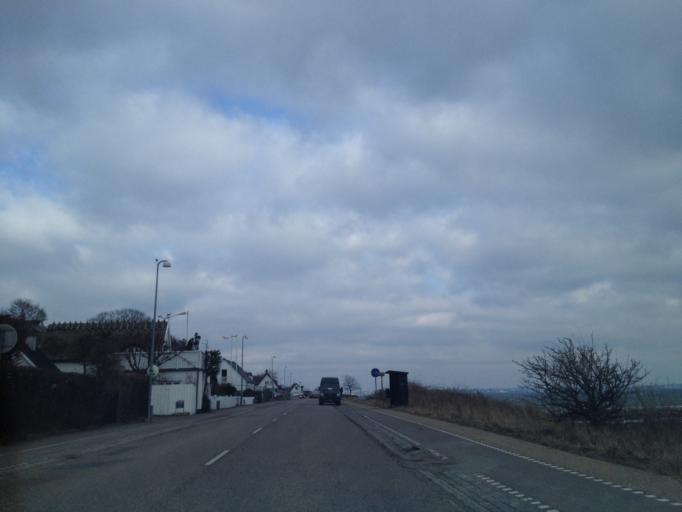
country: DK
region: Capital Region
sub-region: Helsingor Kommune
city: Espergaerde
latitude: 56.0089
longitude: 12.5887
